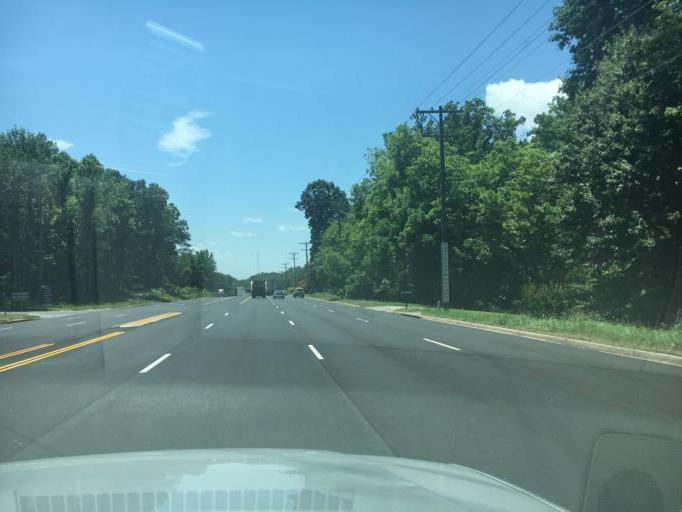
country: US
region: South Carolina
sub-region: Greenville County
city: Travelers Rest
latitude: 34.9294
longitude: -82.4526
